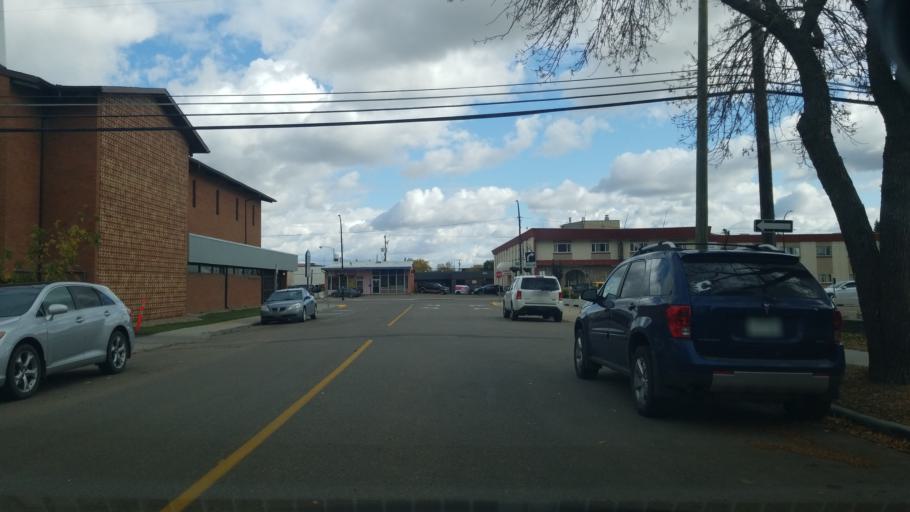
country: CA
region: Saskatchewan
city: Lloydminster
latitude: 53.2807
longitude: -110.0065
